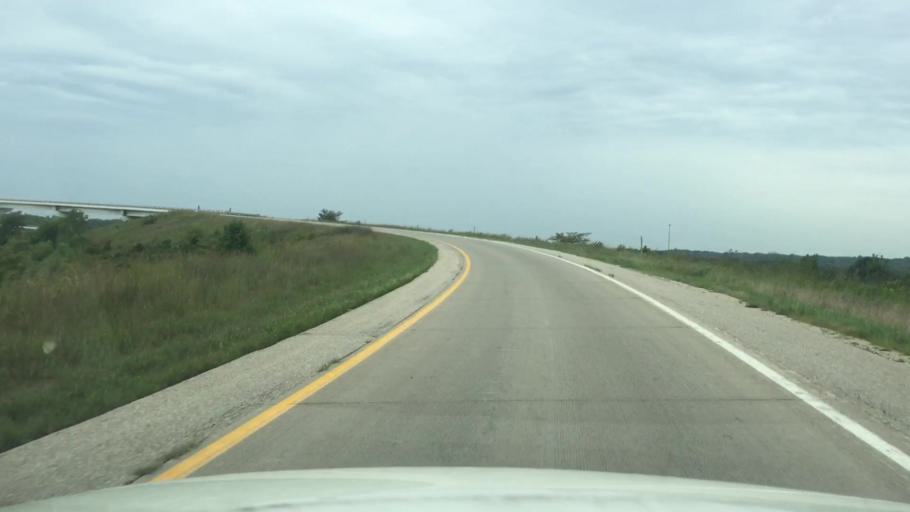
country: US
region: Iowa
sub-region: Polk County
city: West Des Moines
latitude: 41.5247
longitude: -93.7685
